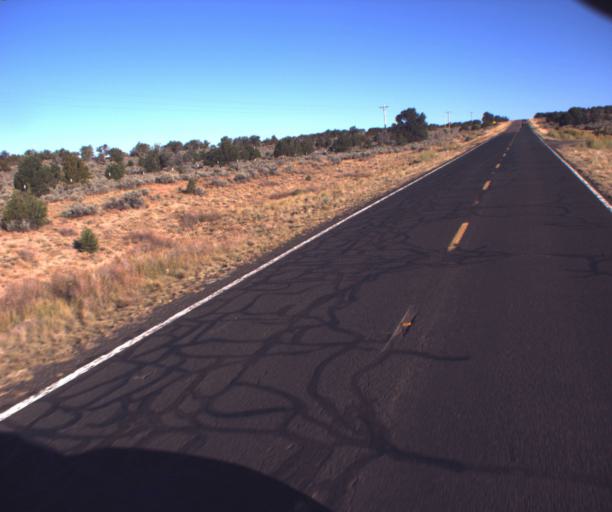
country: US
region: Arizona
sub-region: Apache County
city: Ganado
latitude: 35.6227
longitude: -109.5431
